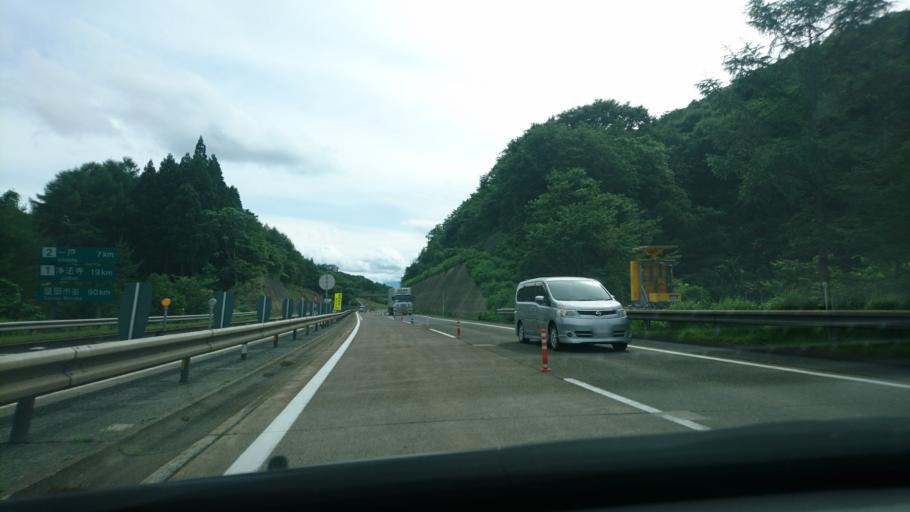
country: JP
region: Iwate
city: Ichinohe
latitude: 40.2282
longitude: 141.3704
